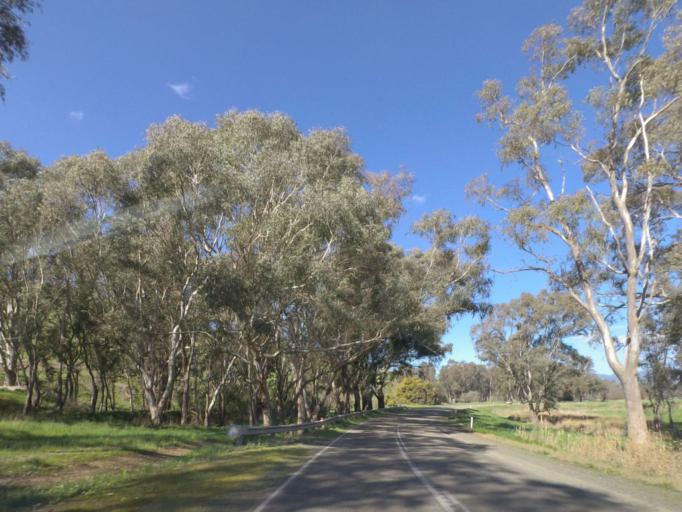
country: AU
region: Victoria
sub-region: Murrindindi
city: Alexandra
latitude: -37.2288
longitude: 145.7625
